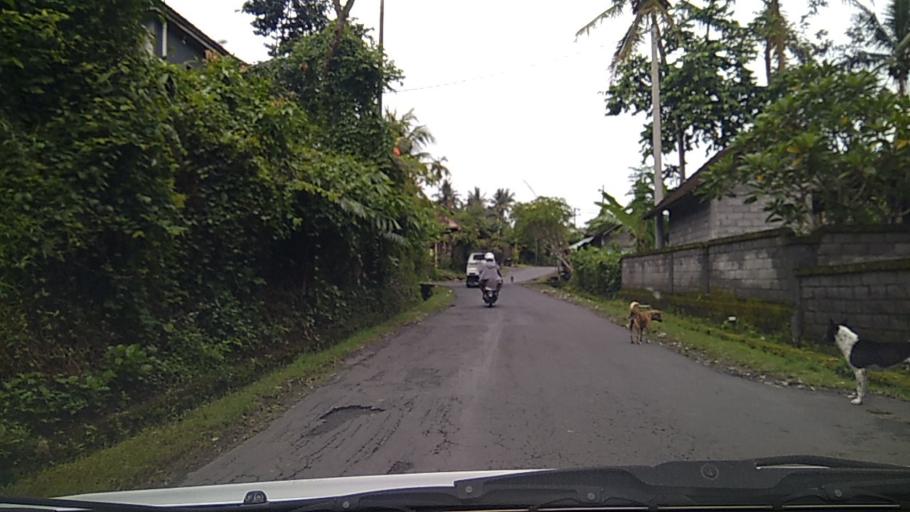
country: ID
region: Bali
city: Banjar Keraman
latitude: -8.5230
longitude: 115.2182
